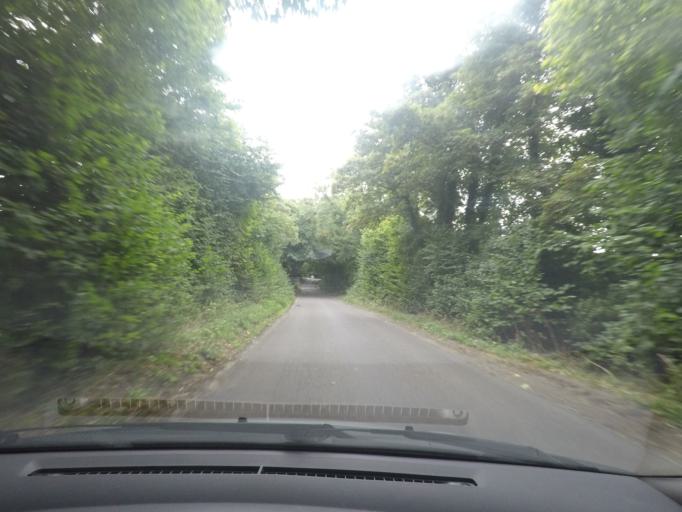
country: GB
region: England
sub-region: Wiltshire
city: Huish
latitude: 51.3497
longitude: -1.7894
